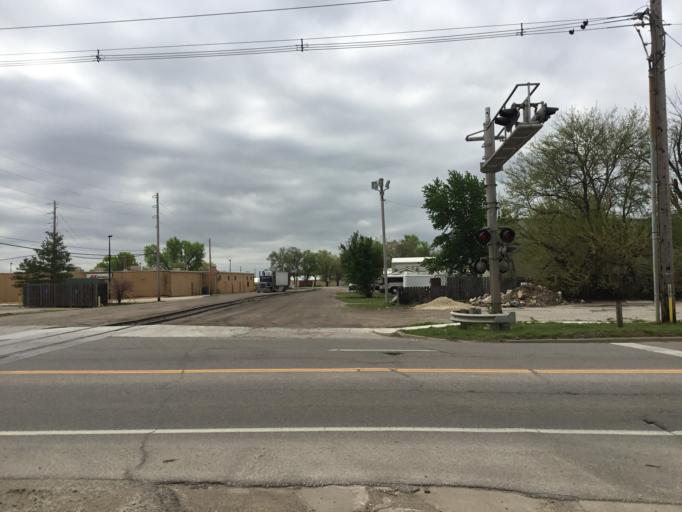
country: US
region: Kansas
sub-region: Butler County
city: El Dorado
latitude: 37.8249
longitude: -96.8514
